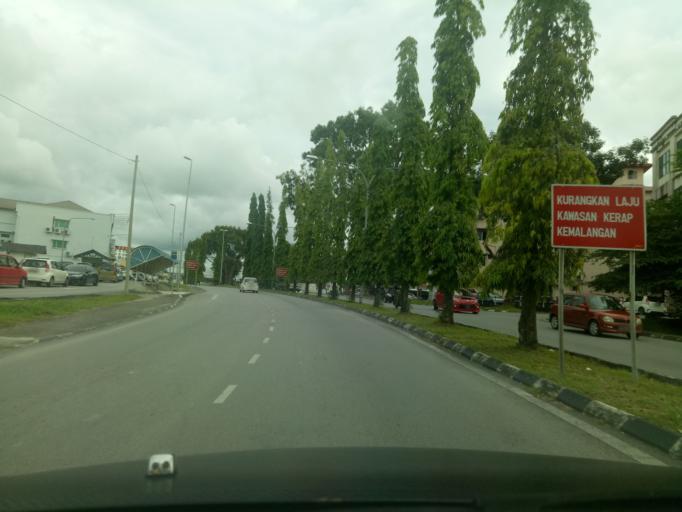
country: MY
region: Sarawak
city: Kuching
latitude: 1.5544
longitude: 110.3813
